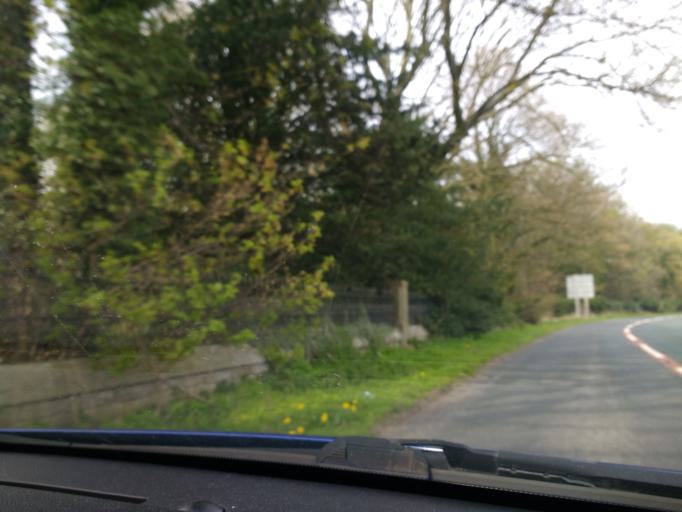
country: GB
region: England
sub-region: Lancashire
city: Lancaster
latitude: 54.0086
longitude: -2.8190
